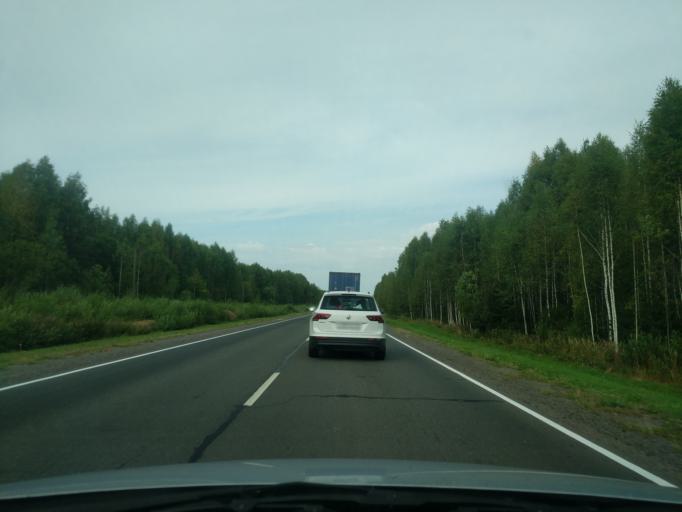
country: RU
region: Kirov
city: Leninskoye
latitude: 58.2845
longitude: 47.2583
